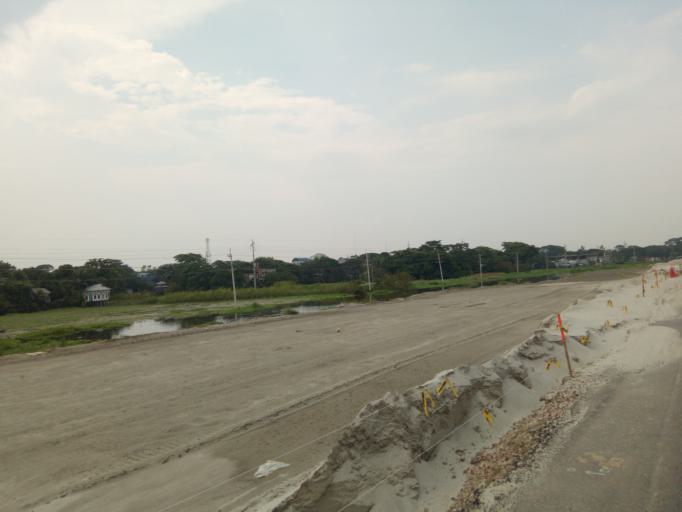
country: BD
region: Dhaka
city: Dohar
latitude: 23.5322
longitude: 90.2906
